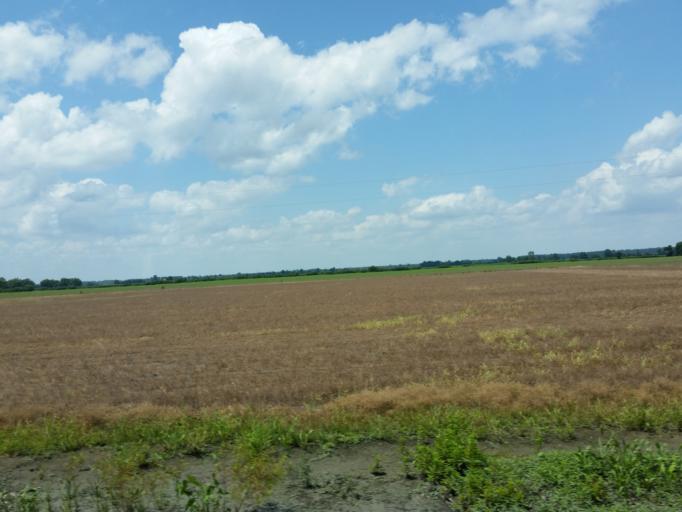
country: US
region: Kentucky
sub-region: Fulton County
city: Hickman
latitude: 36.5370
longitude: -89.3387
